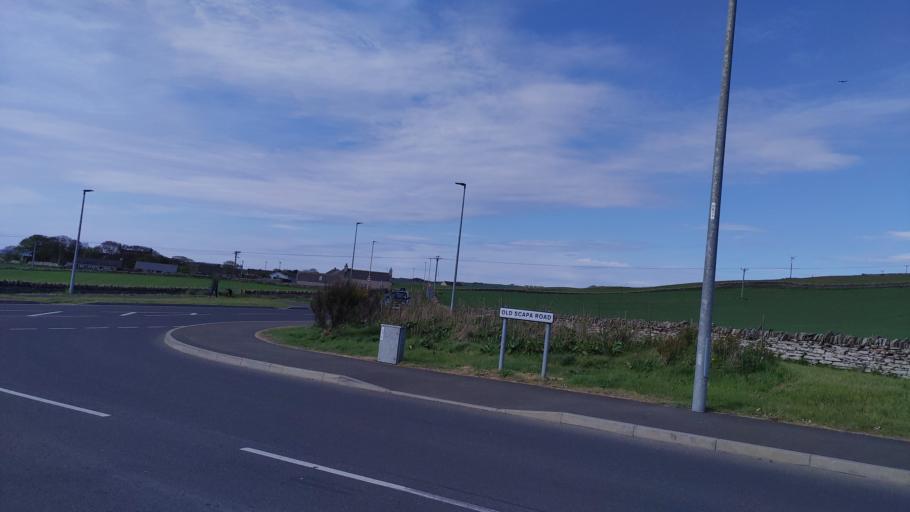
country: GB
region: Scotland
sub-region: Orkney Islands
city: Orkney
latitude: 58.9744
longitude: -2.9707
